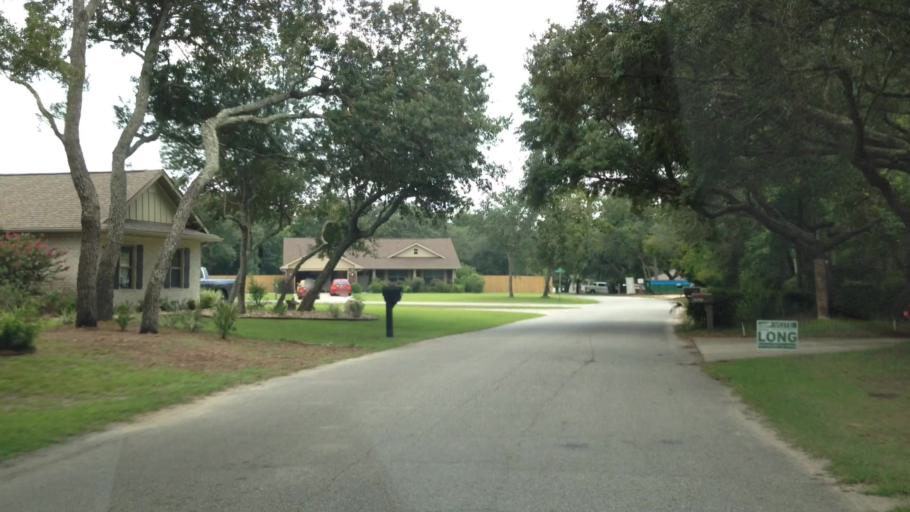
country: US
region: Florida
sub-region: Santa Rosa County
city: Holley
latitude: 30.4426
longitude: -86.9345
